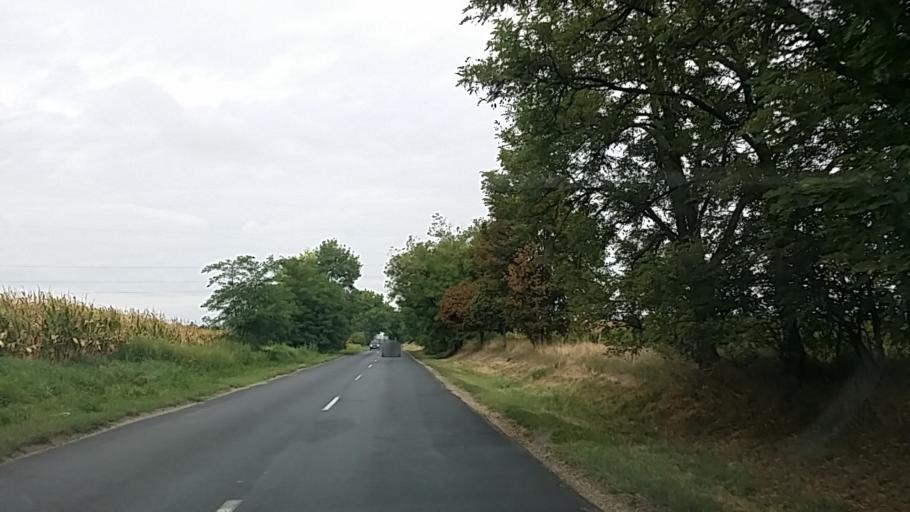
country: HU
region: Komarom-Esztergom
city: Tata
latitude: 47.6575
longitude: 18.2760
